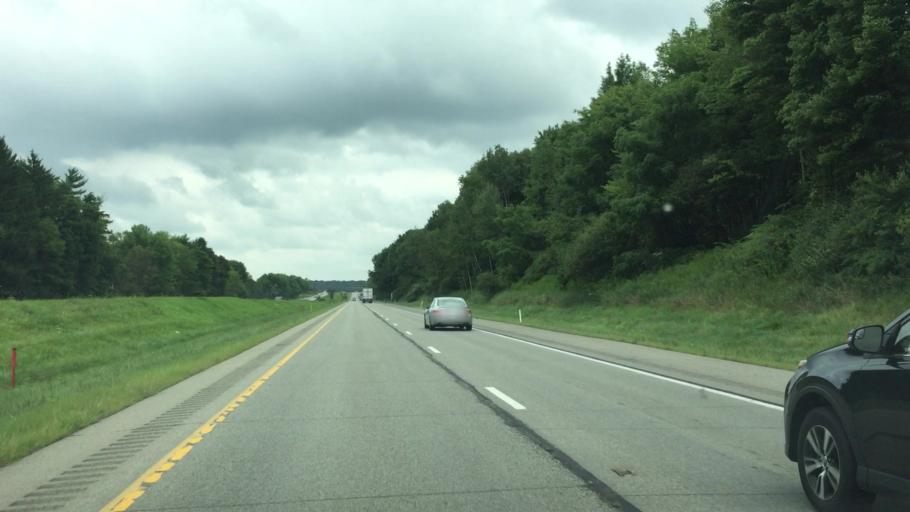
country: US
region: Pennsylvania
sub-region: Butler County
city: Slippery Rock
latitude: 41.0823
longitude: -80.1337
